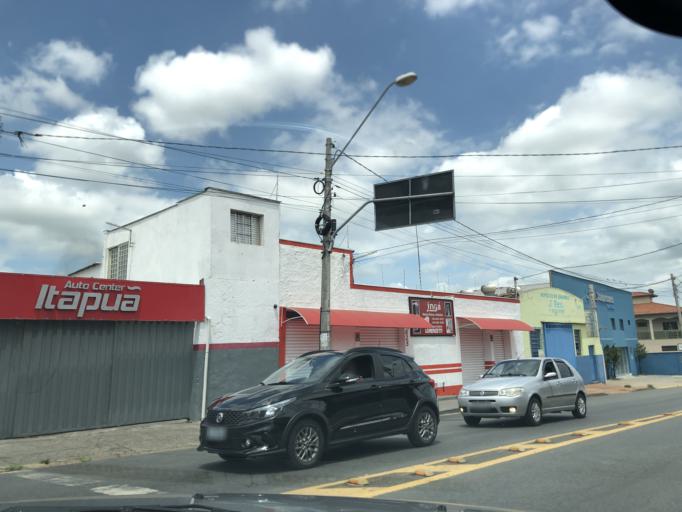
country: BR
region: Sao Paulo
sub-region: Piracicaba
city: Piracicaba
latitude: -22.7507
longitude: -47.6528
